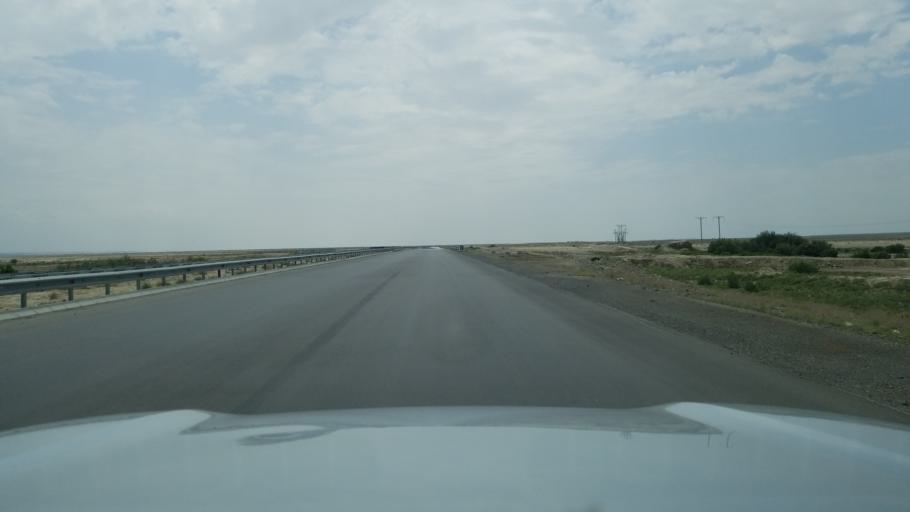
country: TM
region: Balkan
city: Gazanjyk
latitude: 39.2317
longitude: 55.0726
